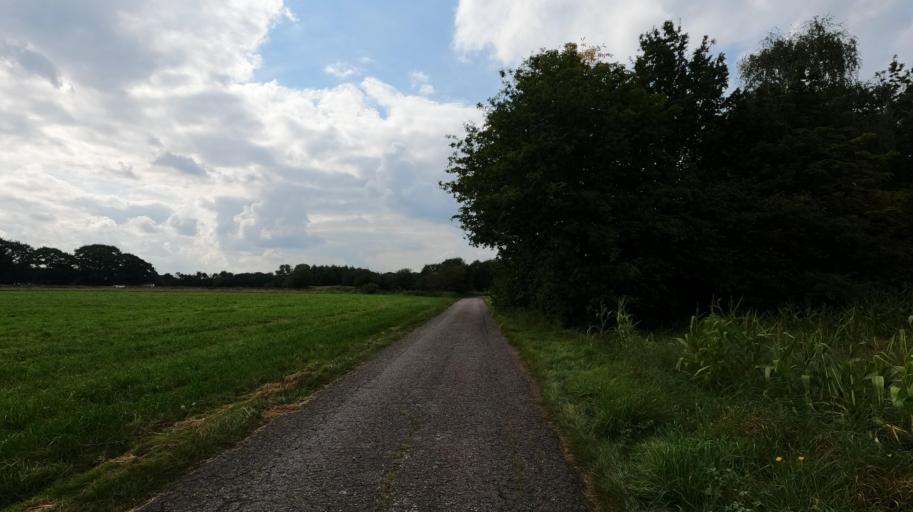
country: BE
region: Flanders
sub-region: Provincie Vlaams-Brabant
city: Keerbergen
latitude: 51.0227
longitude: 4.6666
